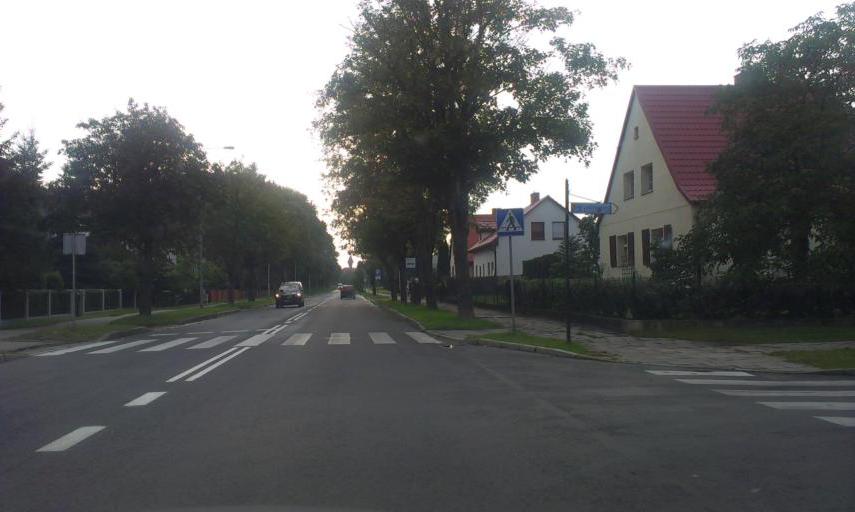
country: PL
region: West Pomeranian Voivodeship
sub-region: Powiat szczecinecki
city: Szczecinek
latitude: 53.7147
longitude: 16.6737
